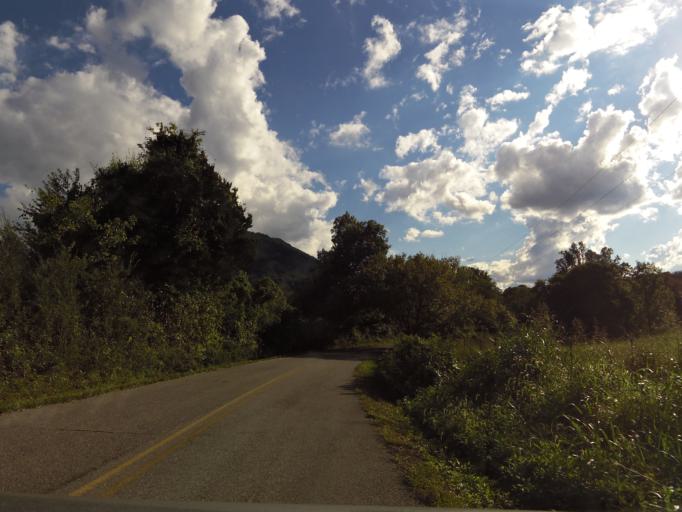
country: US
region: Tennessee
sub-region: Grainger County
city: Blaine
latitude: 36.1355
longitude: -83.7523
